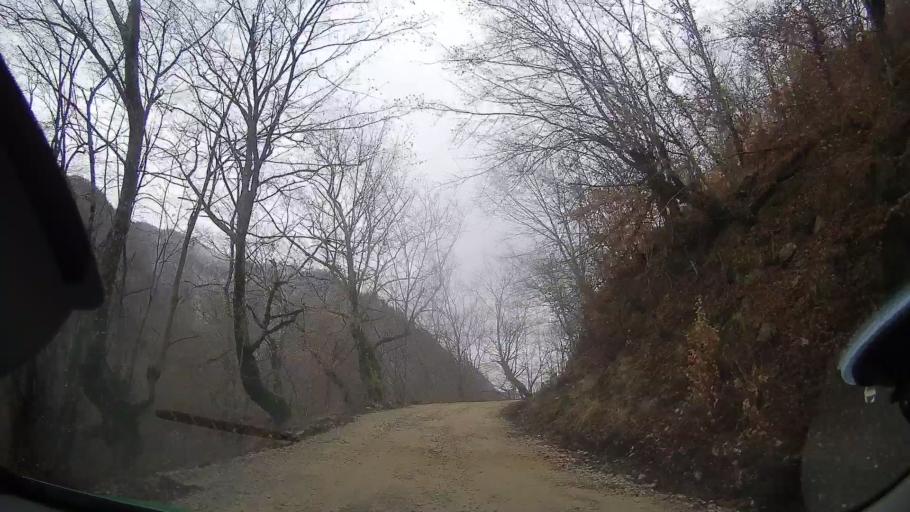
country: RO
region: Cluj
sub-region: Comuna Maguri-Racatau
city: Maguri-Racatau
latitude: 46.6519
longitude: 23.1936
